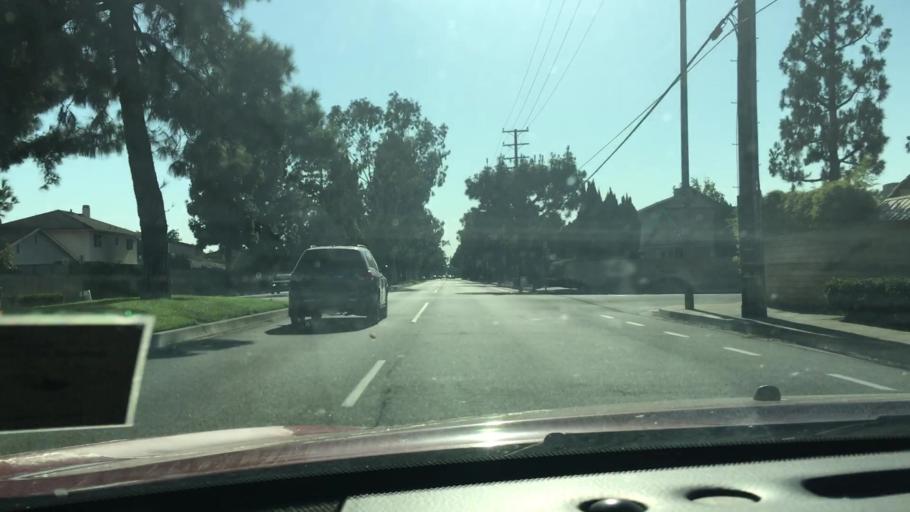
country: US
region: California
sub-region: Orange County
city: La Palma
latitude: 33.8734
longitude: -118.0418
